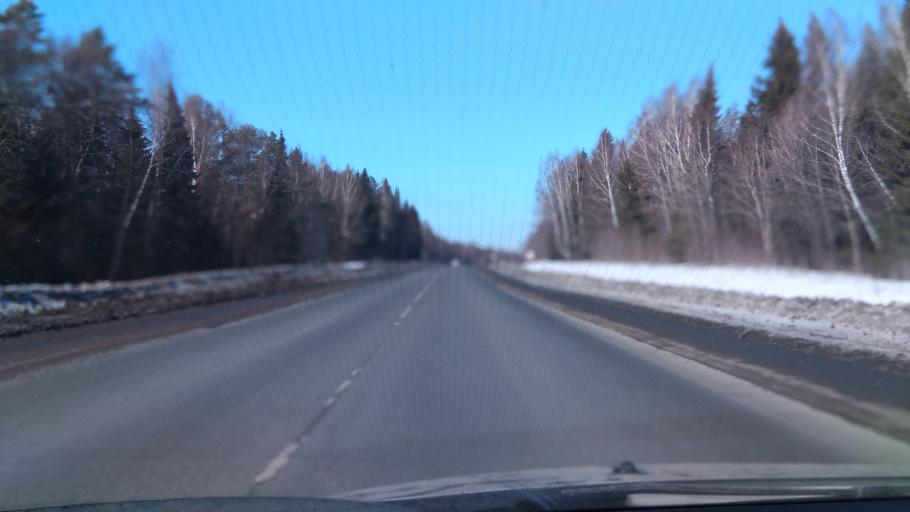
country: RU
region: Perm
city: Kungur
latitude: 57.4245
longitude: 56.8389
